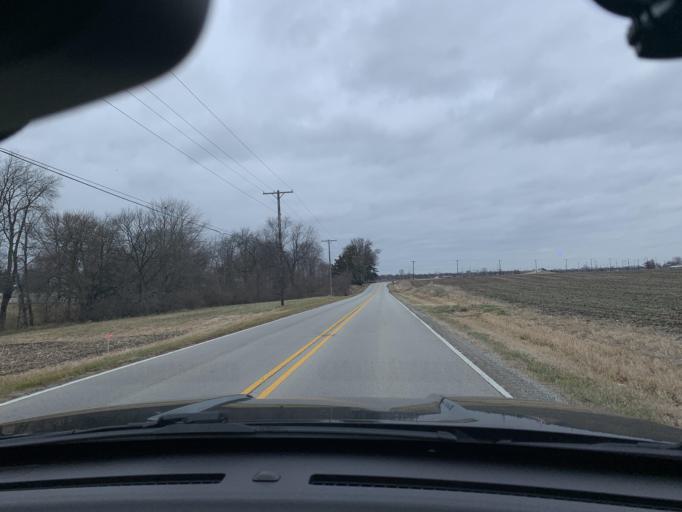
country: US
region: Illinois
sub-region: Sangamon County
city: Jerome
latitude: 39.7326
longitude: -89.6907
